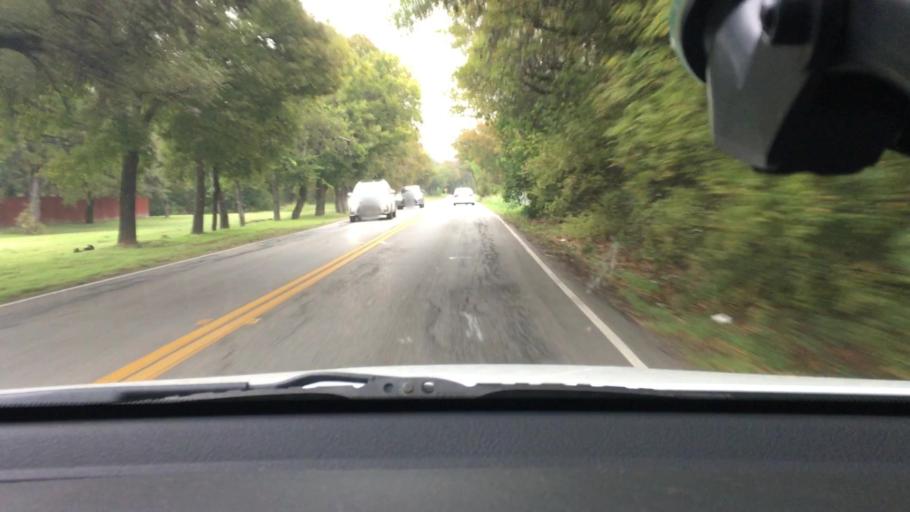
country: US
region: Texas
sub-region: Bexar County
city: Live Oak
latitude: 29.5947
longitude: -98.3626
